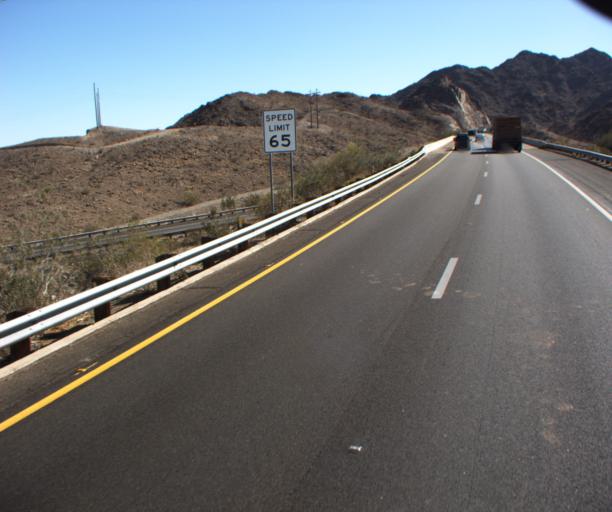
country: US
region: Arizona
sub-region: Yuma County
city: Fortuna Foothills
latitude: 32.6703
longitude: -114.3139
